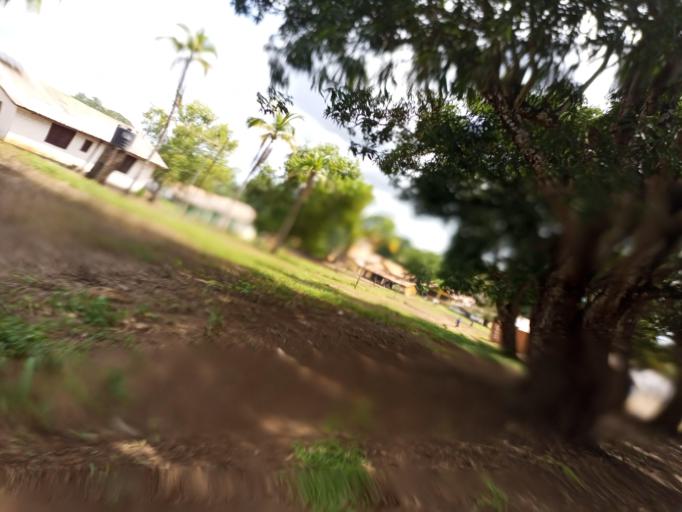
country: SL
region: Northern Province
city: Kamakwie
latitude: 9.4982
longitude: -12.2360
